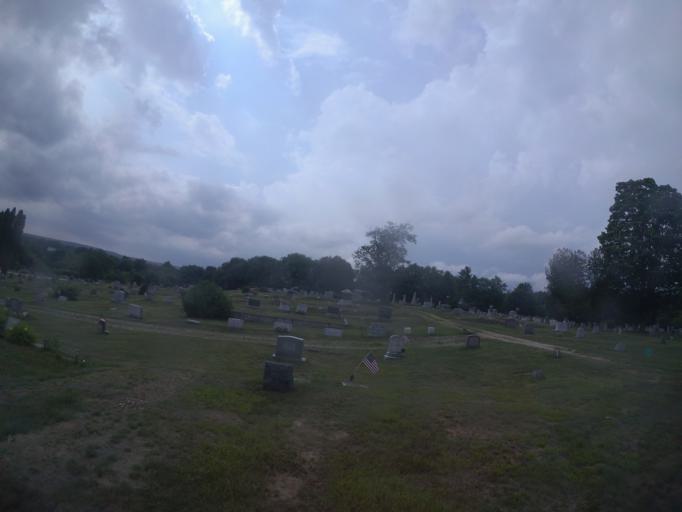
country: US
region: Maine
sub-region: Cumberland County
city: New Gloucester
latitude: 43.8849
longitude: -70.3332
